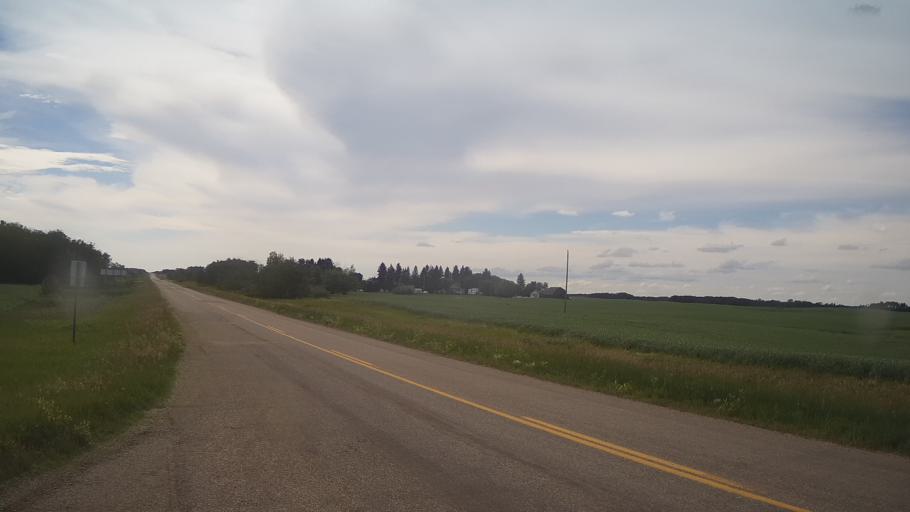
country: CA
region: Saskatchewan
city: Melville
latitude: 51.2102
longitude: -102.8183
